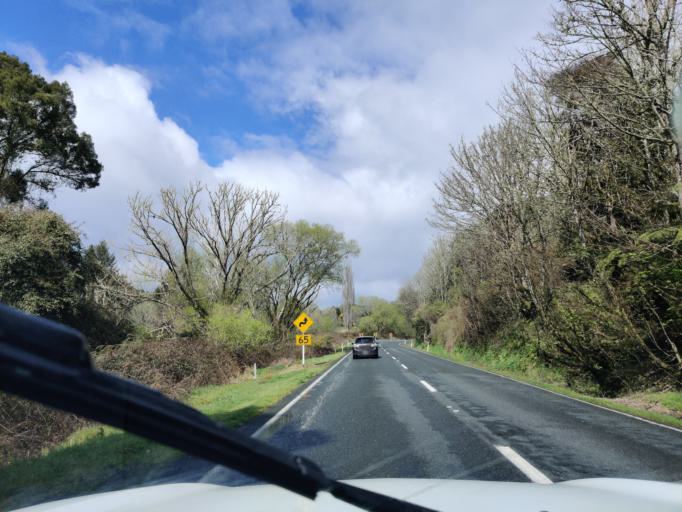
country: NZ
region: Waikato
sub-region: Otorohanga District
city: Otorohanga
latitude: -38.5958
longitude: 175.2190
